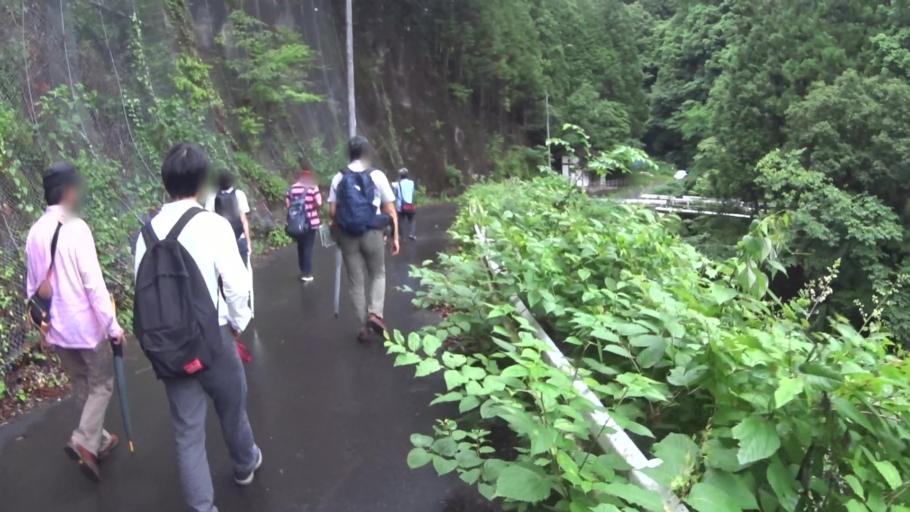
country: JP
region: Tokyo
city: Itsukaichi
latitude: 35.8023
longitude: 139.0784
